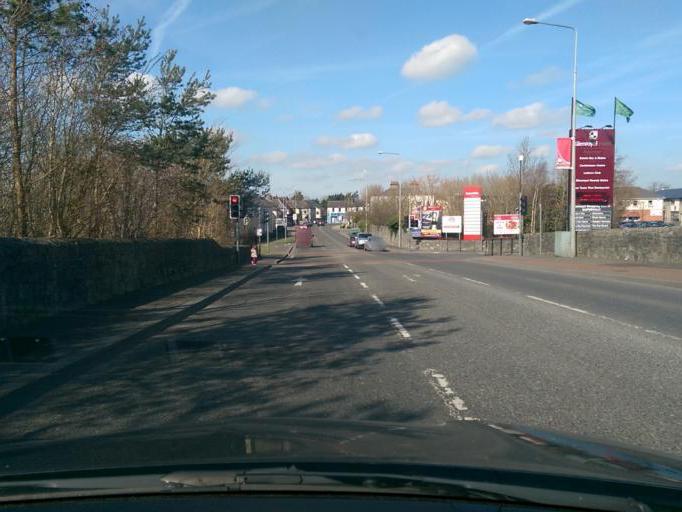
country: IE
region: Leinster
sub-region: Kildare
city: Maynooth
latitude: 53.3799
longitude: -6.5891
